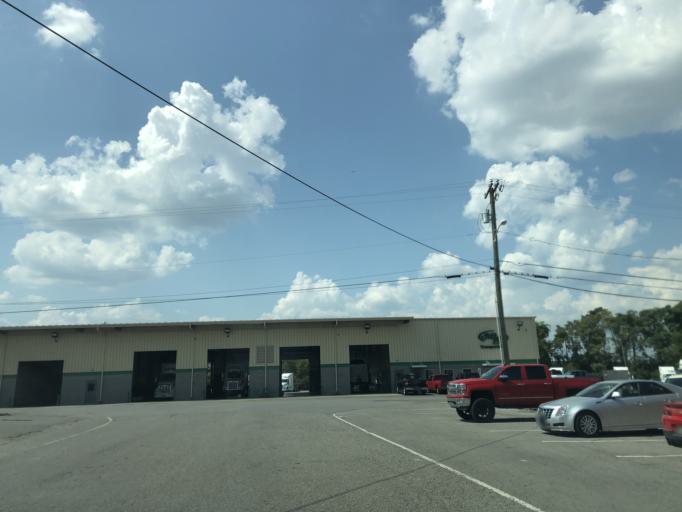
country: US
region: Tennessee
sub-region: Davidson County
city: Nashville
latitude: 36.1325
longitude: -86.7443
